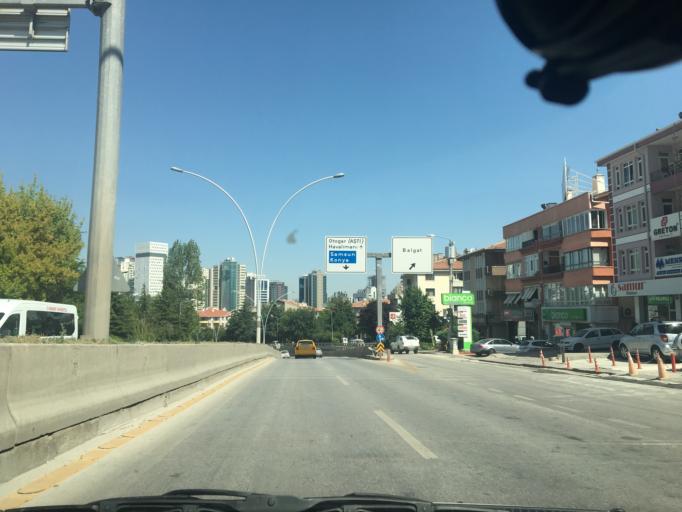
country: TR
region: Ankara
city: Ankara
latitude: 39.8963
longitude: 32.8199
